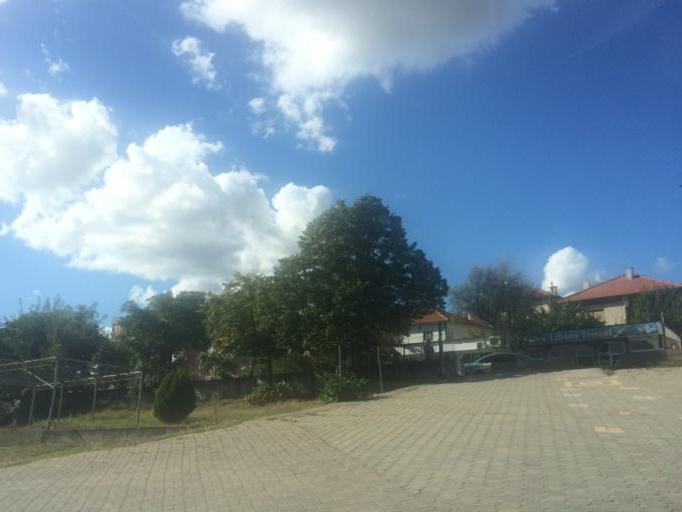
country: MK
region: Kocani
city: Kochani
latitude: 41.9127
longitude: 22.4208
